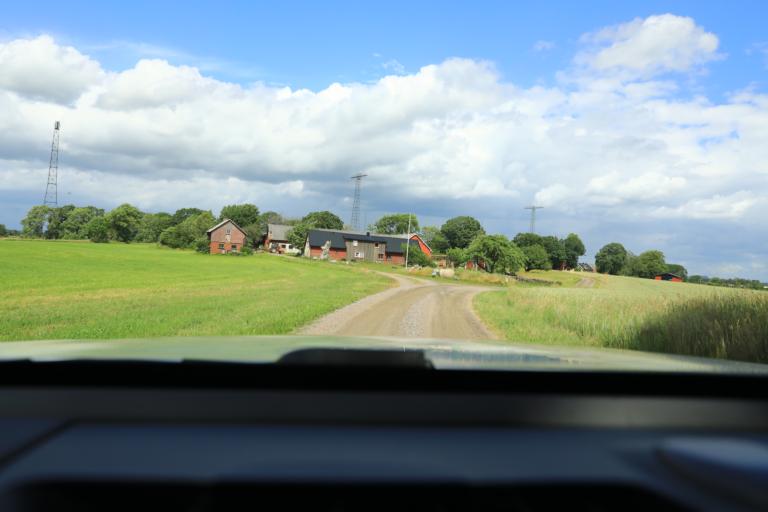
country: SE
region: Halland
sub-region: Varbergs Kommun
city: Tvaaker
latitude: 57.1041
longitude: 12.4021
